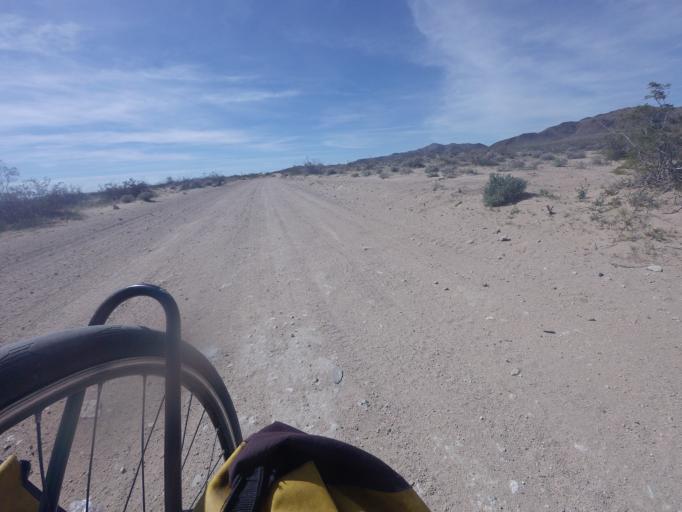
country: US
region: California
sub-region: San Bernardino County
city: Searles Valley
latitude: 35.5742
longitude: -117.4354
